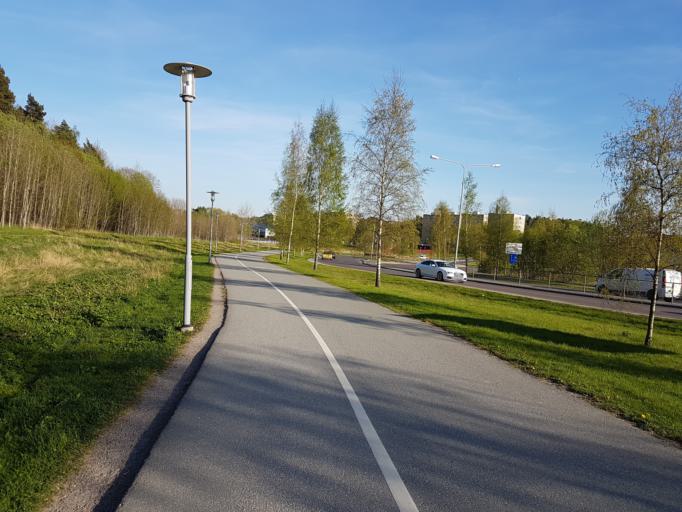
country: SE
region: Stockholm
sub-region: Solna Kommun
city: Rasunda
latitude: 59.3801
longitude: 17.9719
